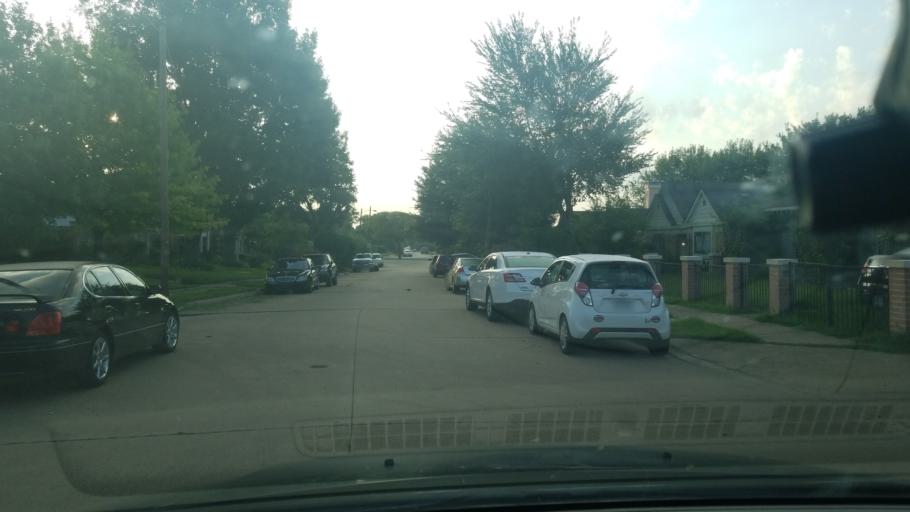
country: US
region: Texas
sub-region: Dallas County
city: Balch Springs
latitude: 32.7285
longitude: -96.6499
